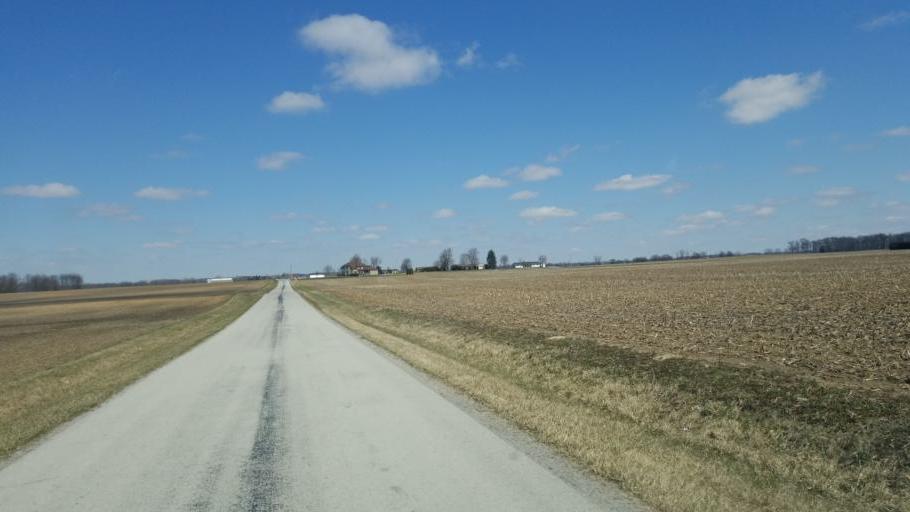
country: US
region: Ohio
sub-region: Wyandot County
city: Upper Sandusky
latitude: 40.7359
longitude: -83.1883
